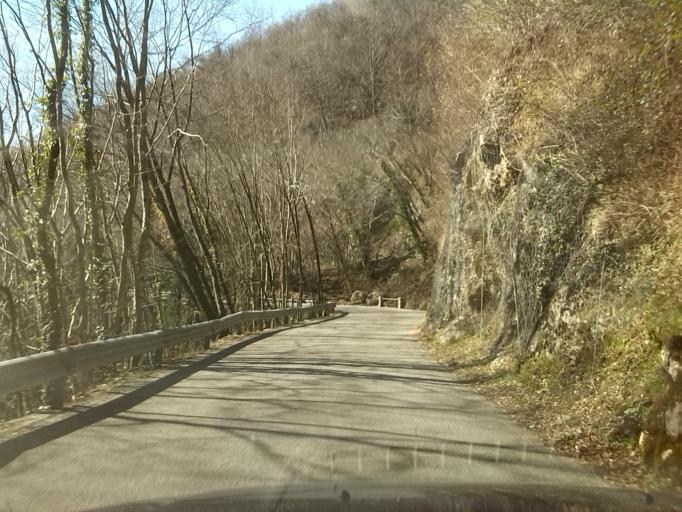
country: IT
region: Friuli Venezia Giulia
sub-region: Provincia di Udine
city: Savogna
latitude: 46.1717
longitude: 13.5583
